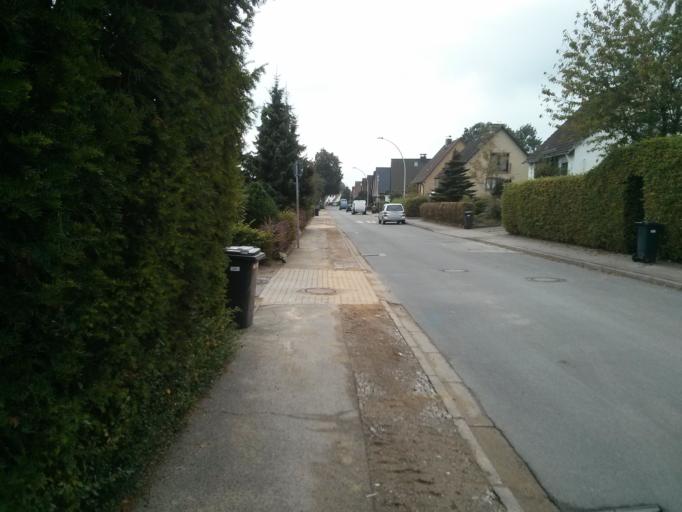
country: DE
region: Schleswig-Holstein
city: Tangstedt
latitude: 53.6544
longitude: 9.8370
